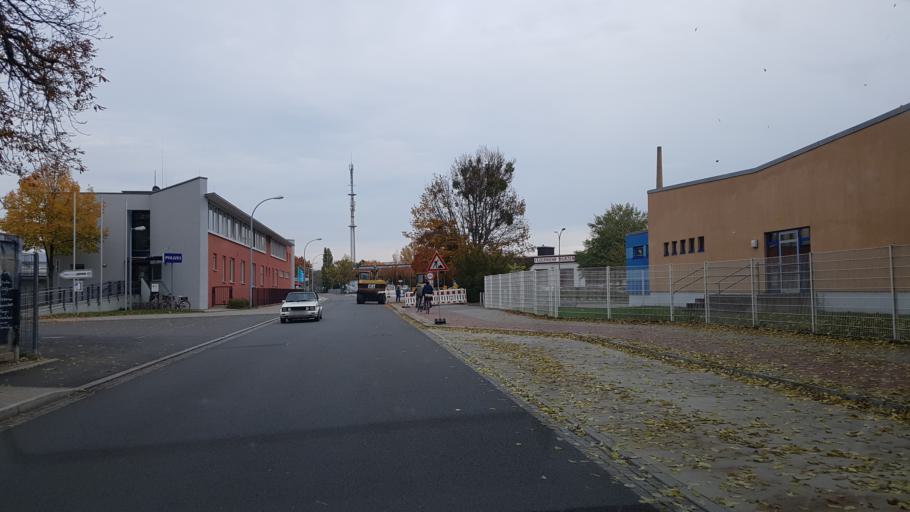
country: DE
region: Saxony
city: Wurzen
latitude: 51.3760
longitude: 12.7480
